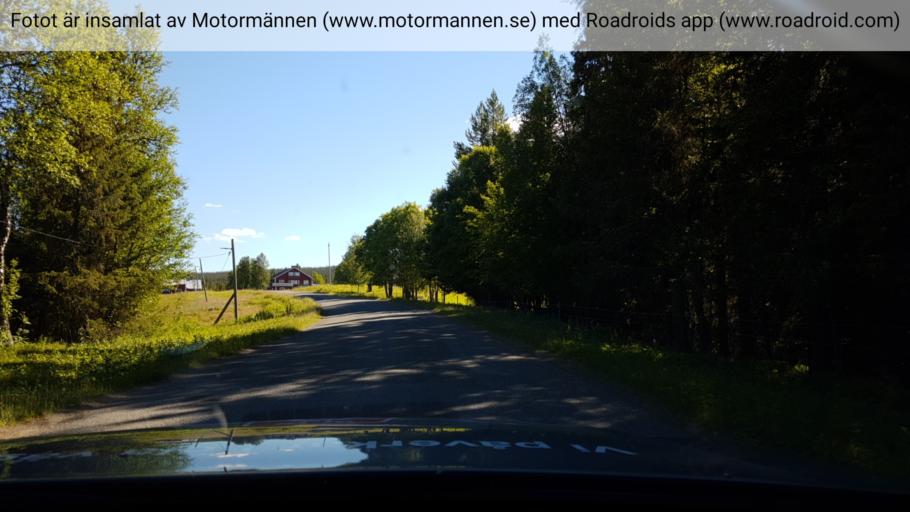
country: SE
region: Jaemtland
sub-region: Are Kommun
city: Are
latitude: 63.1592
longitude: 13.0719
